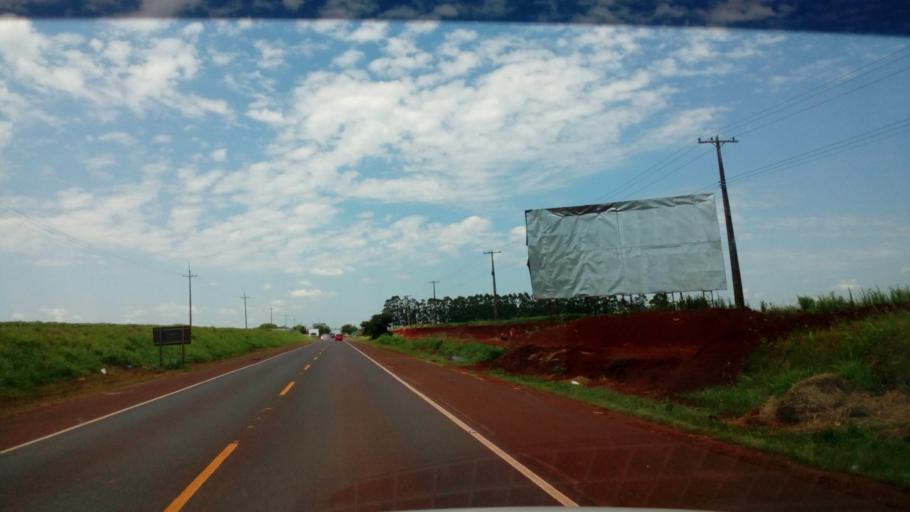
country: PY
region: Alto Parana
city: Santa Rita
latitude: -25.7422
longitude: -55.0502
